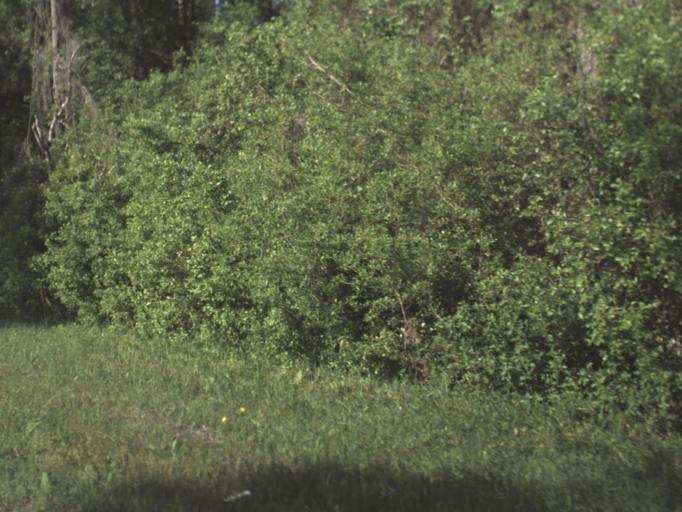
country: US
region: Florida
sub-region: Gulf County
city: Wewahitchka
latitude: 30.0312
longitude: -84.9836
